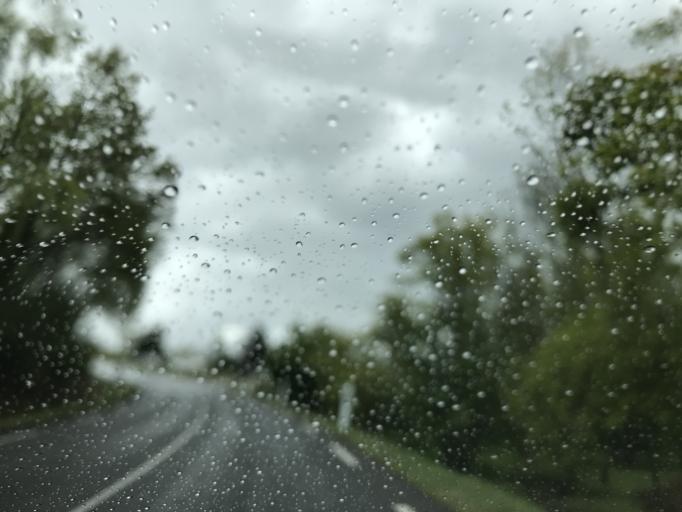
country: FR
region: Auvergne
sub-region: Departement du Puy-de-Dome
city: Montaigut
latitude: 45.6960
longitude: 3.4297
